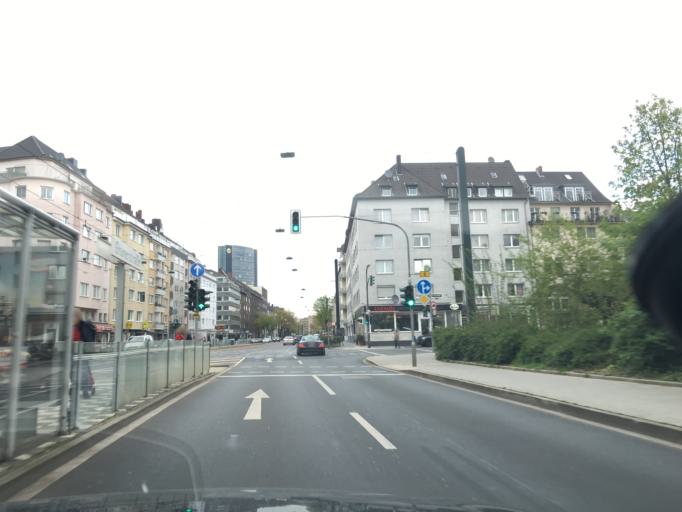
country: DE
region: North Rhine-Westphalia
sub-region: Regierungsbezirk Dusseldorf
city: Dusseldorf
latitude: 51.2430
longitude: 6.8019
